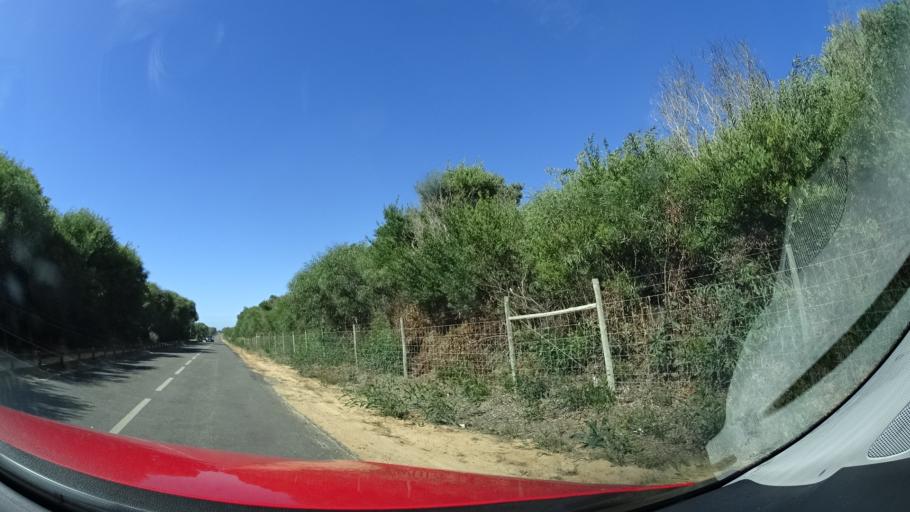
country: PT
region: Beja
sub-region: Odemira
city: Sao Teotonio
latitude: 37.5362
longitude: -8.7848
